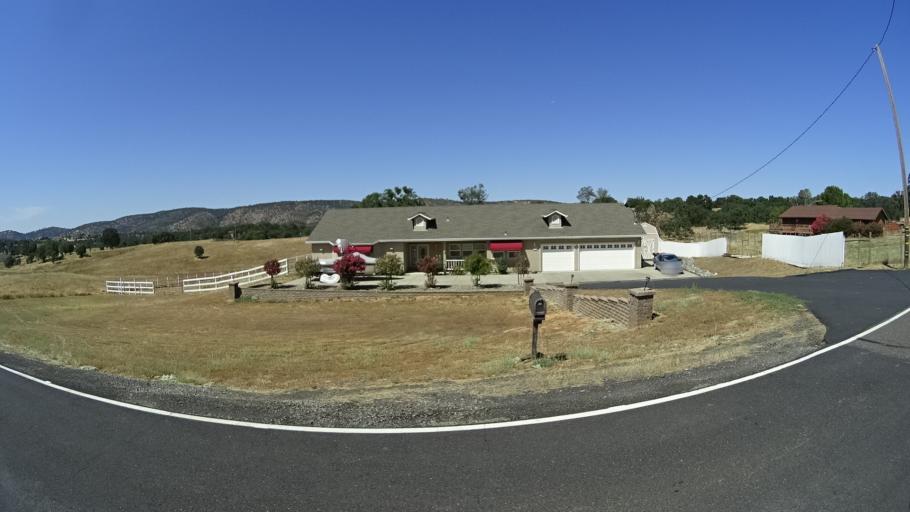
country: US
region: California
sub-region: Calaveras County
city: Copperopolis
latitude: 37.9376
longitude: -120.6445
